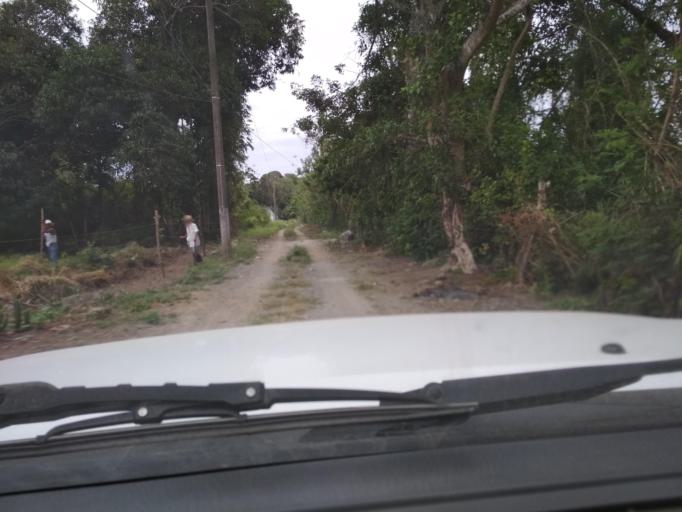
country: MX
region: Veracruz
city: El Tejar
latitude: 19.0731
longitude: -96.1390
